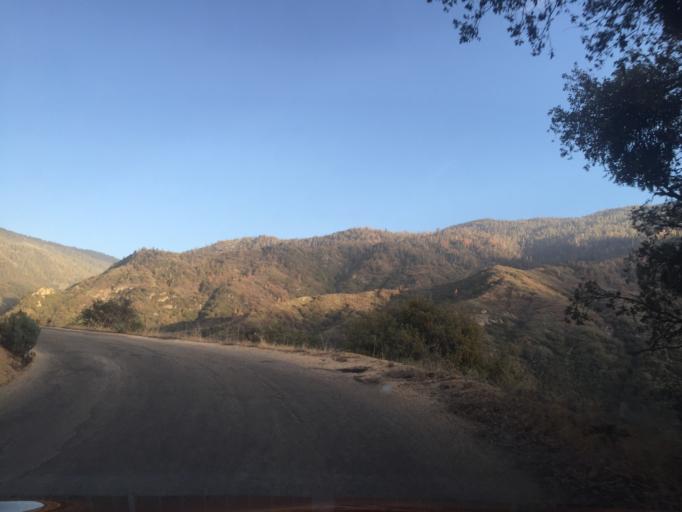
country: US
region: California
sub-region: Tulare County
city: Three Rivers
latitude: 36.4306
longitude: -118.7478
